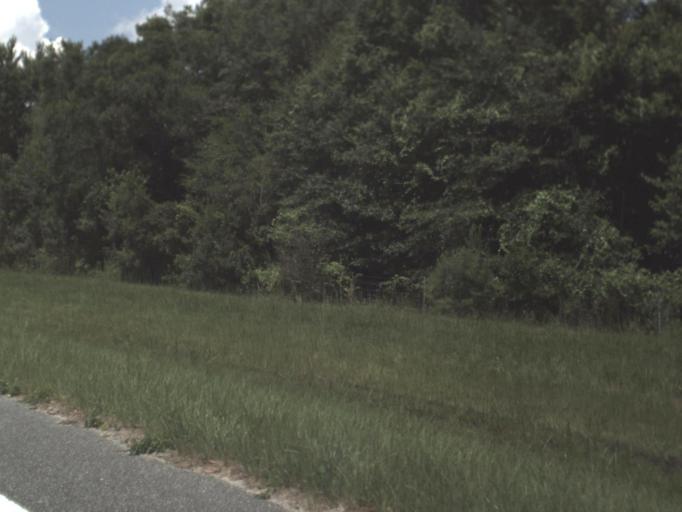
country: US
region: Florida
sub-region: Bradford County
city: Starke
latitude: 30.0159
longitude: -82.0496
